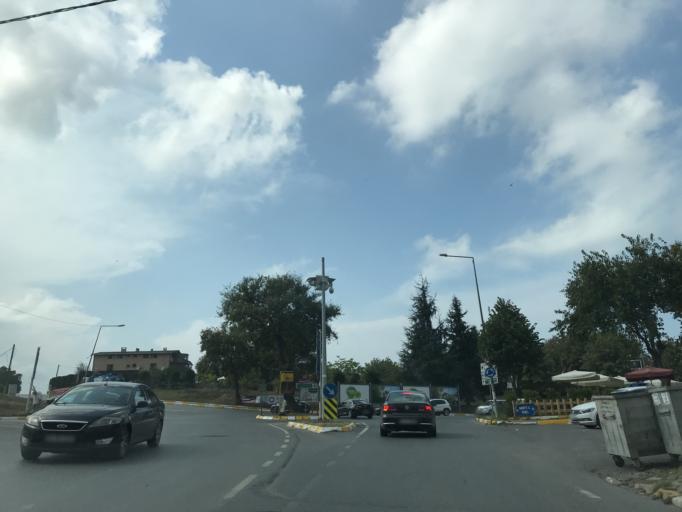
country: TR
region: Istanbul
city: Arikoey
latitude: 41.2198
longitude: 29.0332
